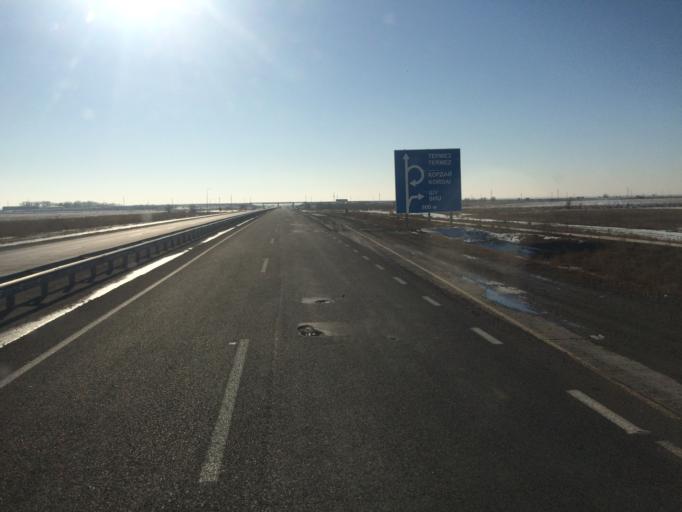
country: KG
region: Chuy
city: Sokuluk
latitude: 43.2827
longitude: 74.2368
